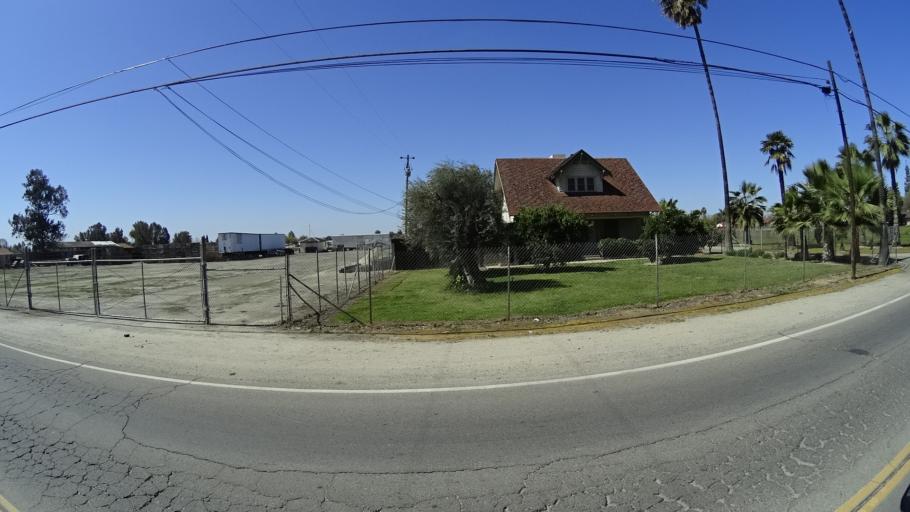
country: US
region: California
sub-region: Fresno County
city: West Park
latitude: 36.7600
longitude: -119.8444
